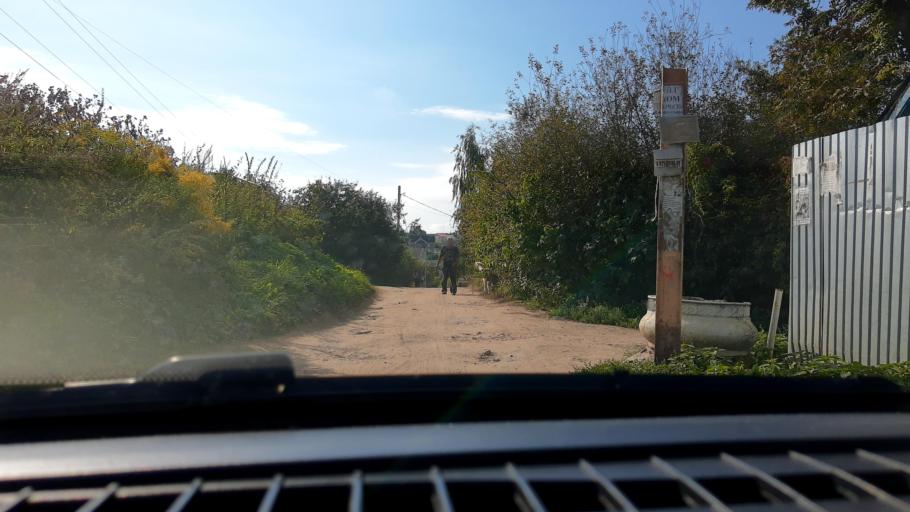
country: RU
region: Nizjnij Novgorod
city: Afonino
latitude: 56.2623
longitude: 44.0915
